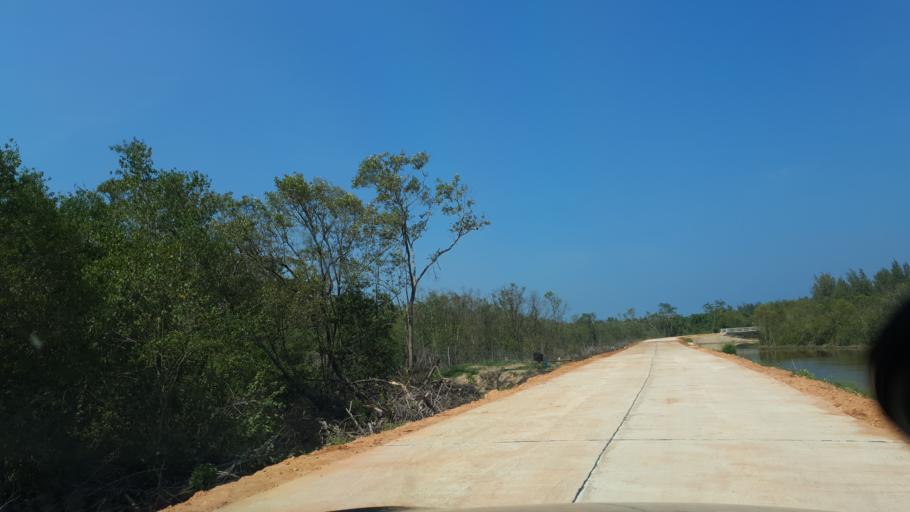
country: TH
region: Surat Thani
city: Tha Chana
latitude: 9.5925
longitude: 99.2077
